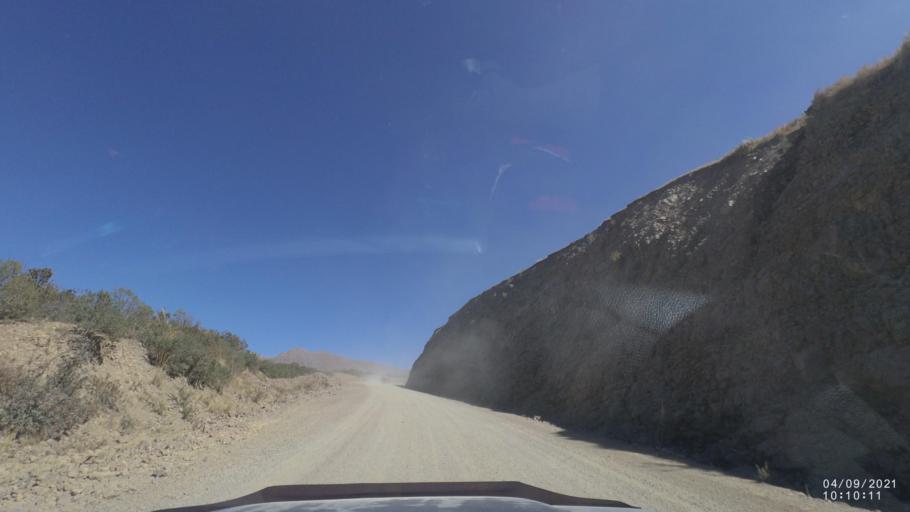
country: BO
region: Cochabamba
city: Sipe Sipe
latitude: -17.3435
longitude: -66.3962
